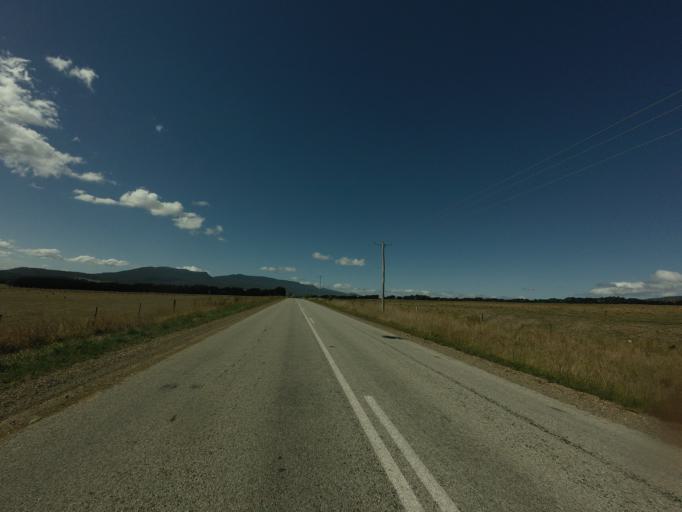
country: AU
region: Tasmania
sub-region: Break O'Day
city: St Helens
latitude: -41.6106
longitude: 148.0187
